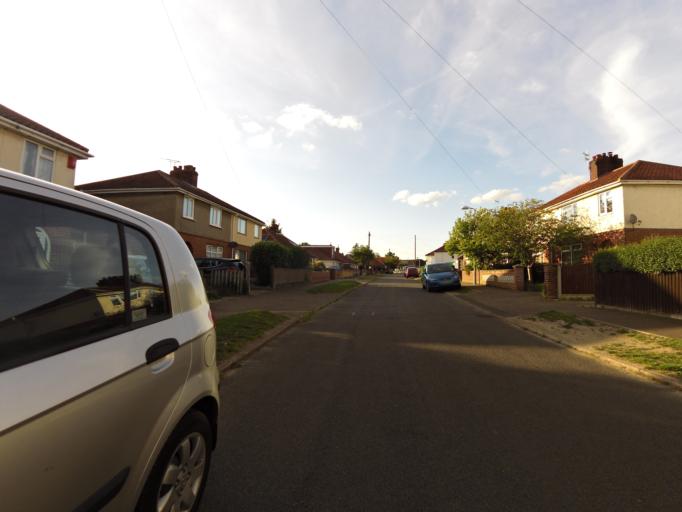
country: GB
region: England
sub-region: Norfolk
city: Norwich
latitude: 52.6574
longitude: 1.2722
